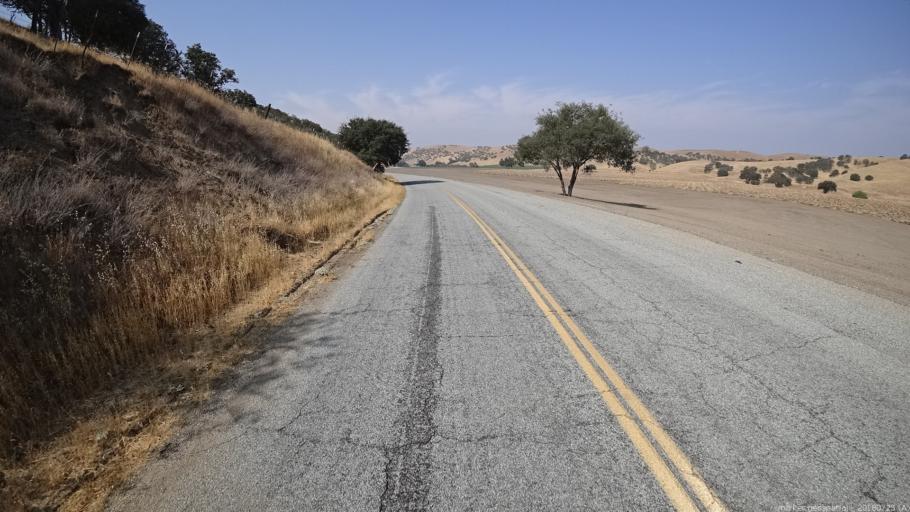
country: US
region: California
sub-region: San Luis Obispo County
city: San Miguel
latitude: 35.8182
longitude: -120.6599
